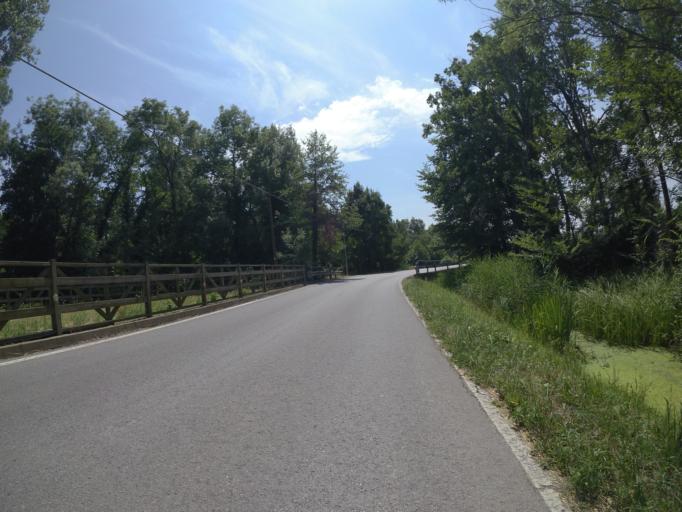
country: IT
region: Friuli Venezia Giulia
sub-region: Provincia di Udine
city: Teor
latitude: 45.8707
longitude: 13.0824
